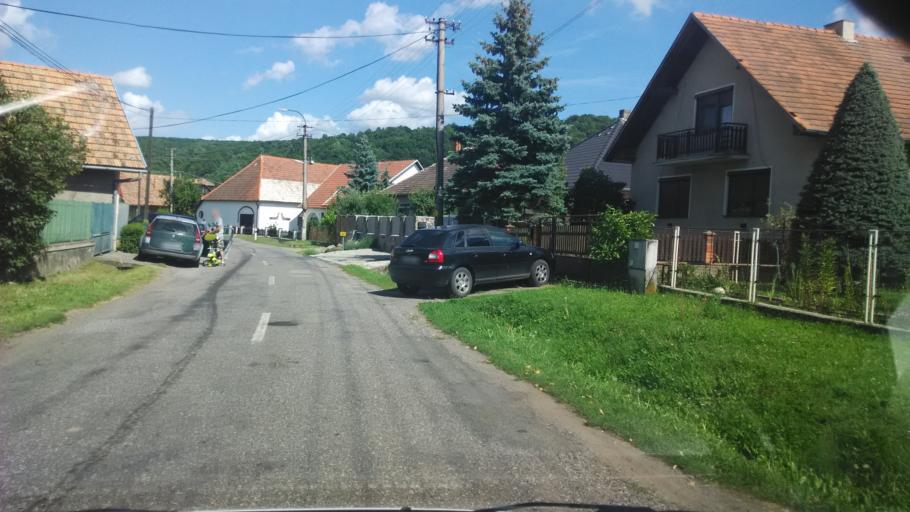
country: SK
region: Banskobystricky
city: Dudince
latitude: 48.2958
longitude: 18.7688
